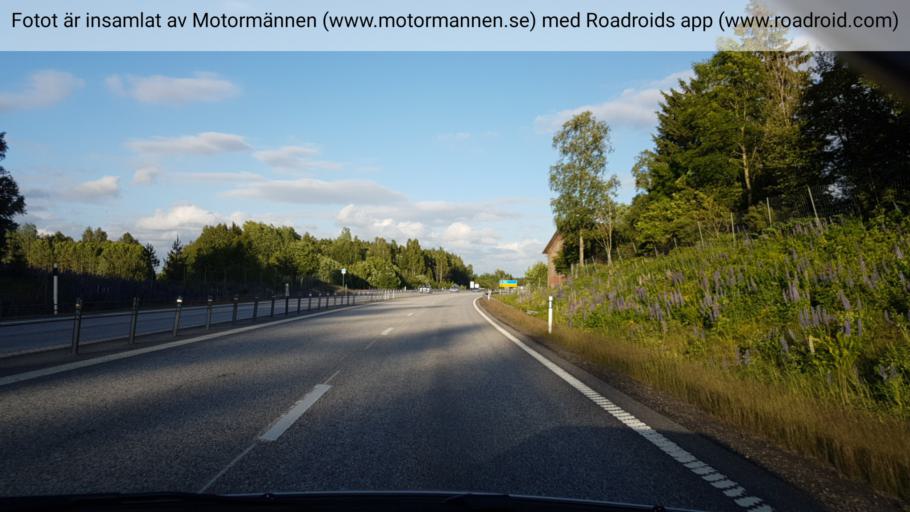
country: SE
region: OErebro
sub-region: Degerfors Kommun
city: Degerfors
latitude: 59.3241
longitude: 14.3801
